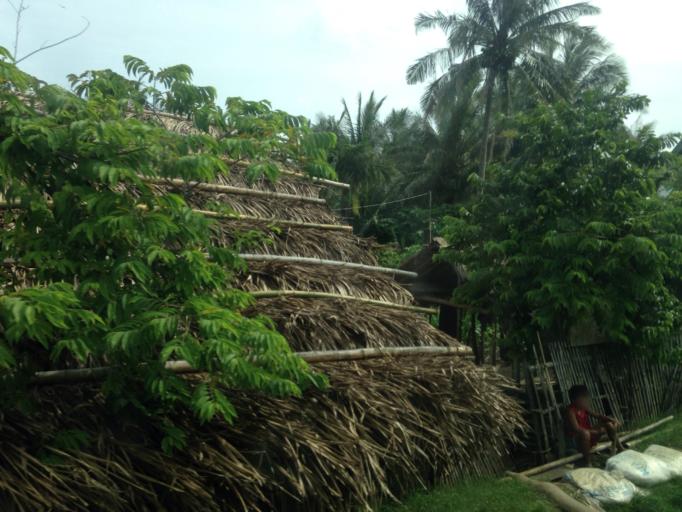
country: PH
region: Mimaropa
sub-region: Province of Mindoro Oriental
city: Manaul
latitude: 12.4052
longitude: 121.3793
